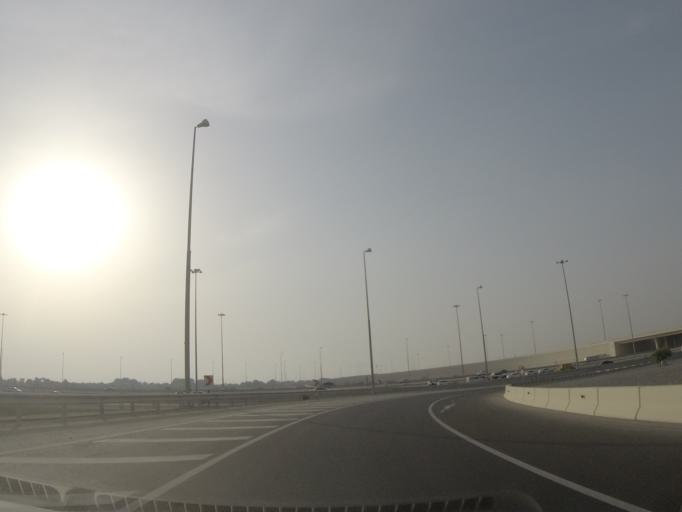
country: AE
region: Abu Dhabi
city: Abu Dhabi
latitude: 24.6918
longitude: 54.7792
